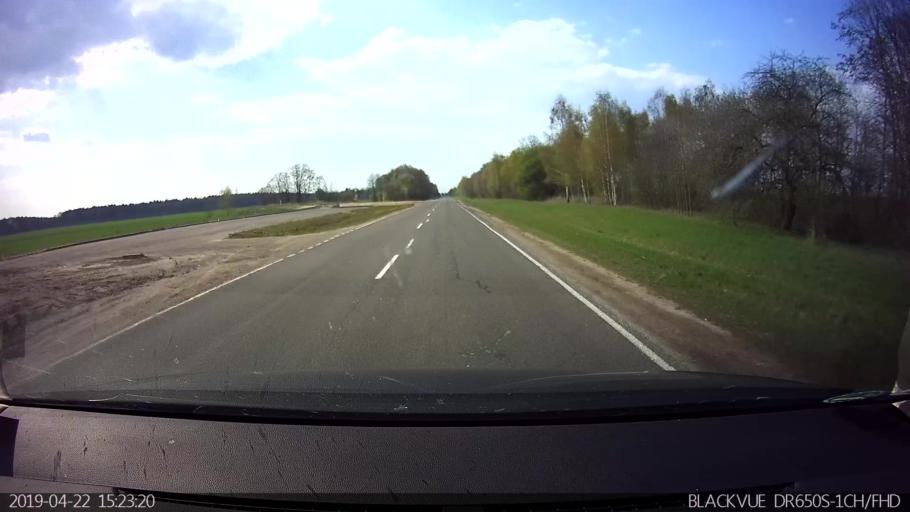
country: BY
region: Brest
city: Vysokaye
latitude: 52.3545
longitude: 23.4287
